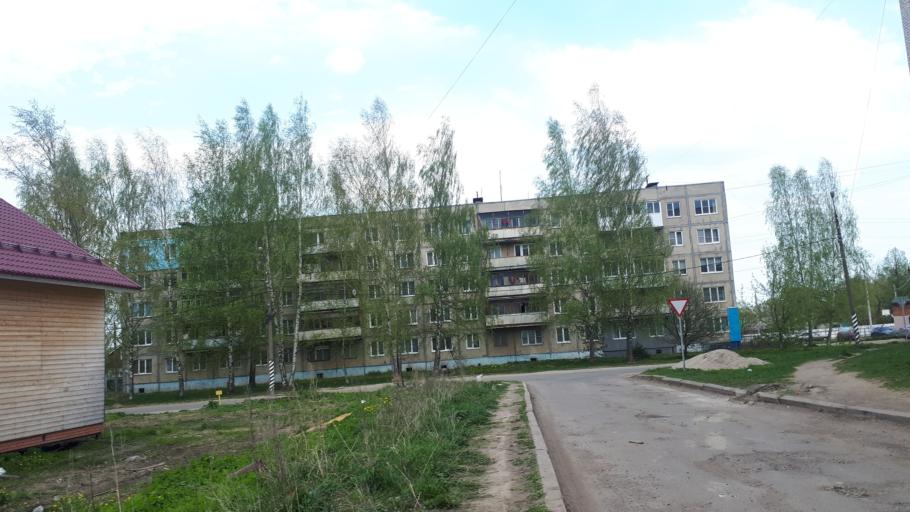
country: RU
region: Jaroslavl
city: Konstantinovskiy
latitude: 57.8314
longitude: 39.5902
